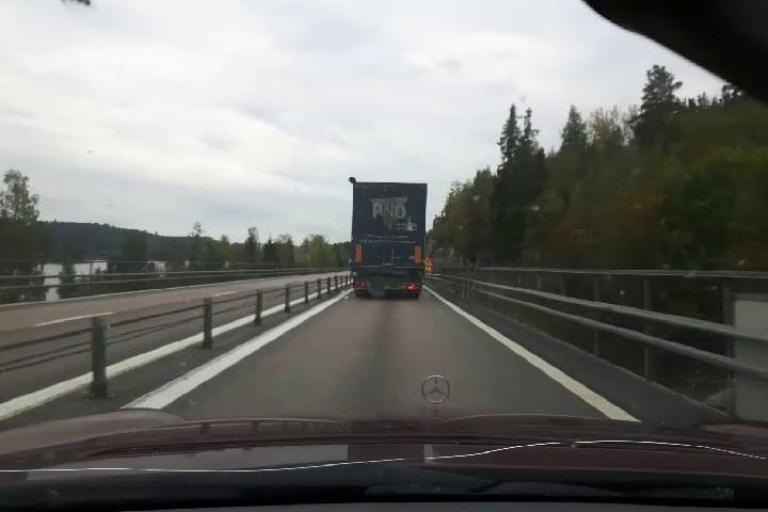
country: SE
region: Vaesternorrland
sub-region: Haernoesands Kommun
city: Haernoesand
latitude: 62.8224
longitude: 17.9700
